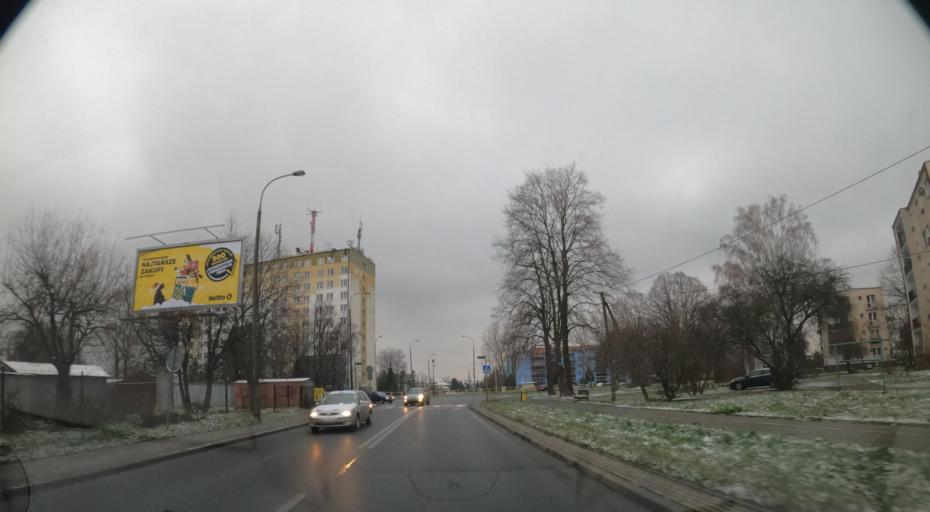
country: PL
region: Masovian Voivodeship
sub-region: Plock
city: Plock
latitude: 52.5519
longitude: 19.6740
